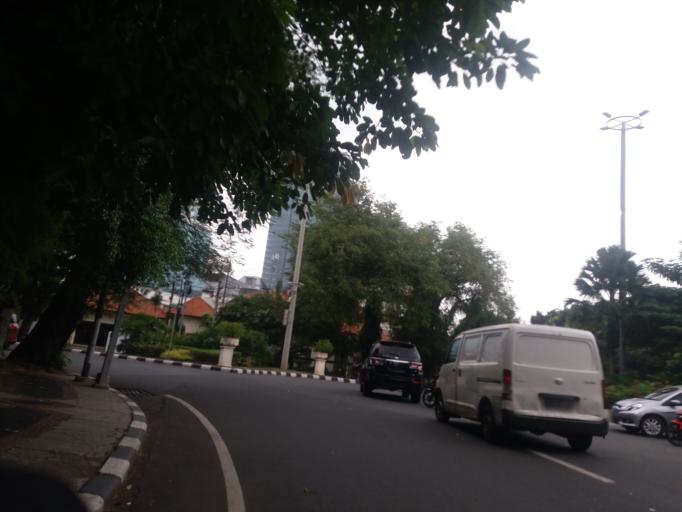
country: ID
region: Jakarta Raya
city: Jakarta
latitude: -6.1883
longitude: 106.8331
